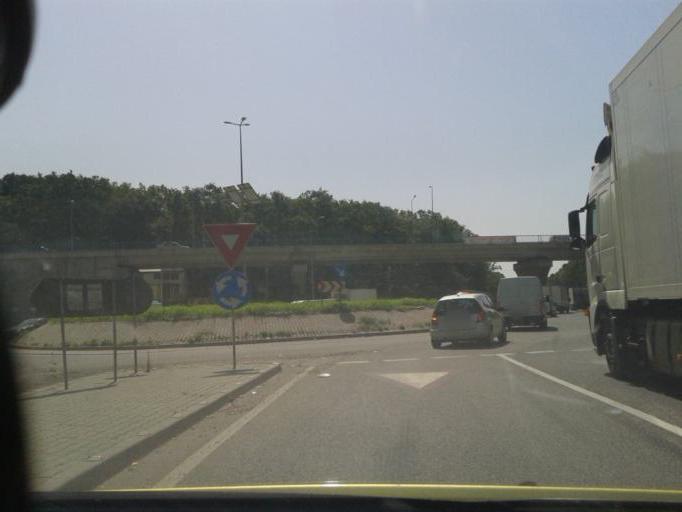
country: RO
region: Ilfov
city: Stefanestii de Jos
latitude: 44.5129
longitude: 26.1874
